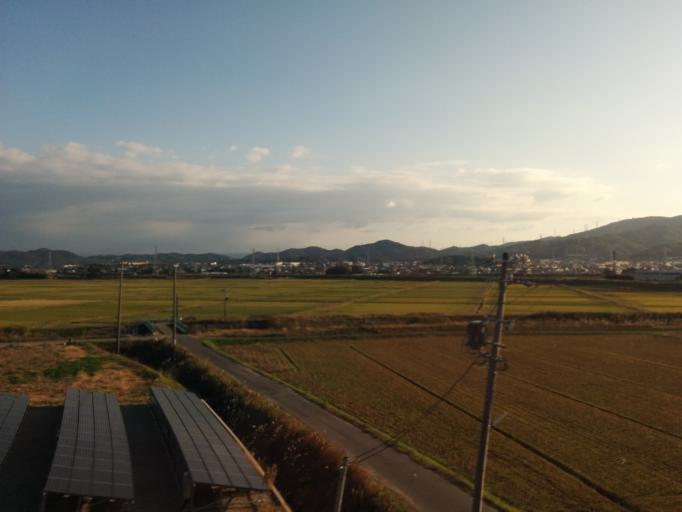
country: JP
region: Aichi
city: Okazaki
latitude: 34.8692
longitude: 137.1523
